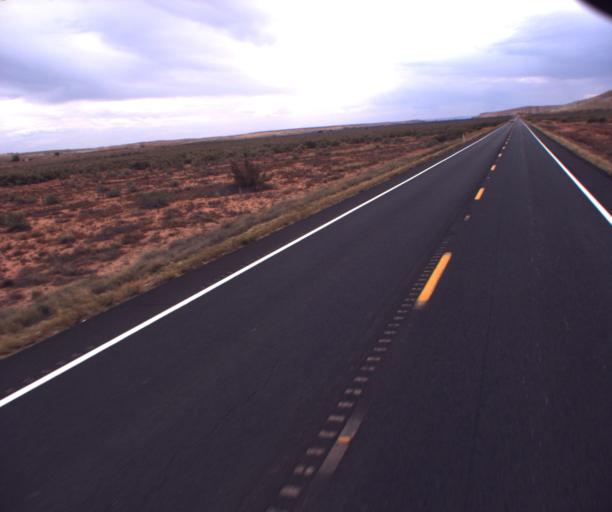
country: US
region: Arizona
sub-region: Coconino County
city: Kaibito
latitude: 36.3443
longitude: -110.9148
